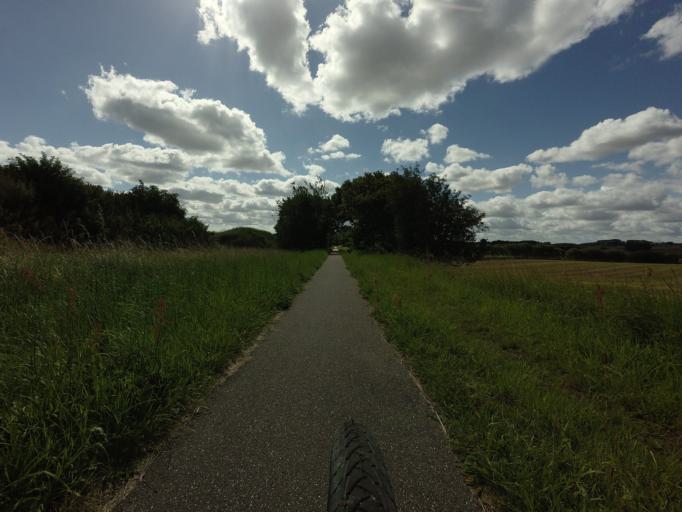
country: DK
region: Central Jutland
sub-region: Horsens Kommune
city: Horsens
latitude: 55.9169
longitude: 9.7685
